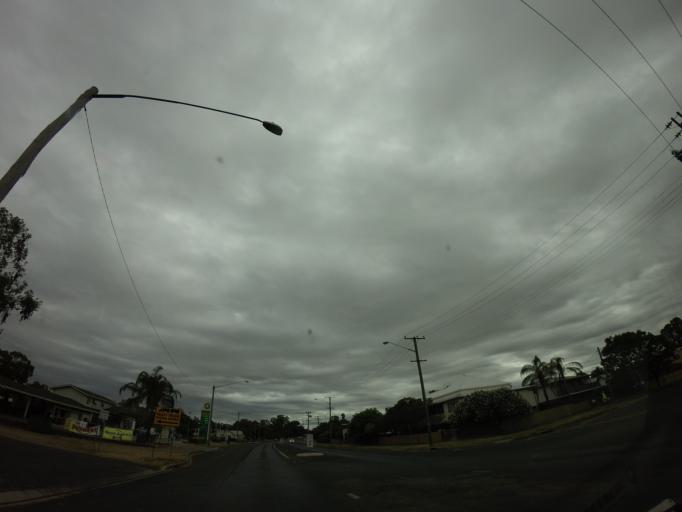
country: AU
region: New South Wales
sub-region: Narrabri
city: Narrabri
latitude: -30.3355
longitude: 149.7698
